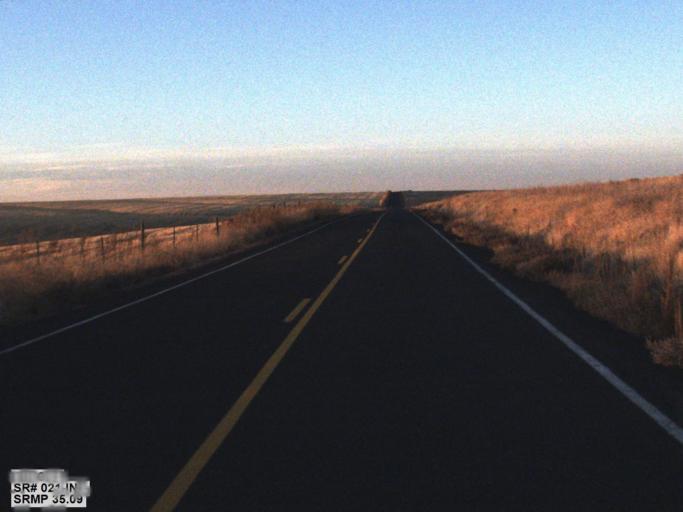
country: US
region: Washington
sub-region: Adams County
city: Ritzville
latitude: 47.0585
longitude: -118.6630
